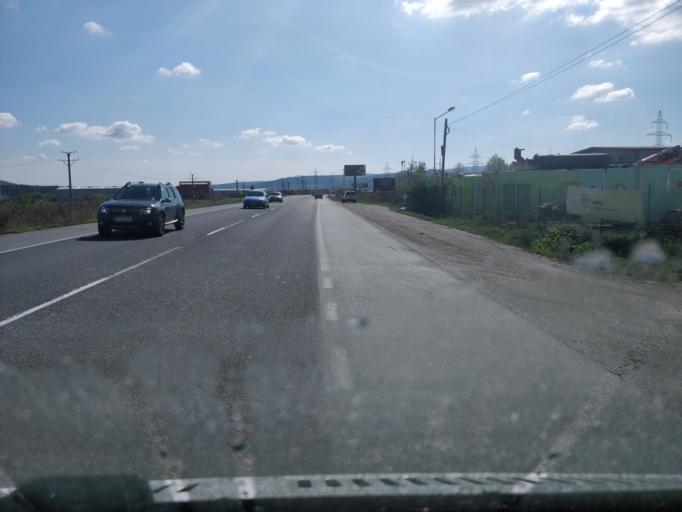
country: RO
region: Cluj
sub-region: Comuna Floresti
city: Luna de Sus
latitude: 46.7505
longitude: 23.4391
